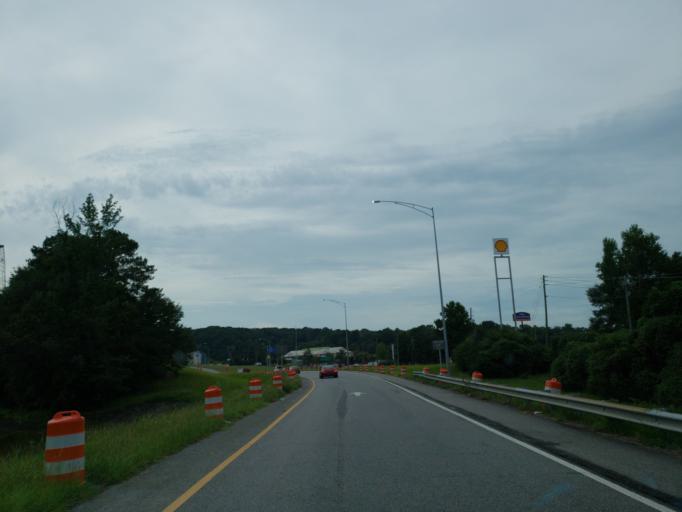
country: US
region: Alabama
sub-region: Tuscaloosa County
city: Holt
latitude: 33.1740
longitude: -87.4709
